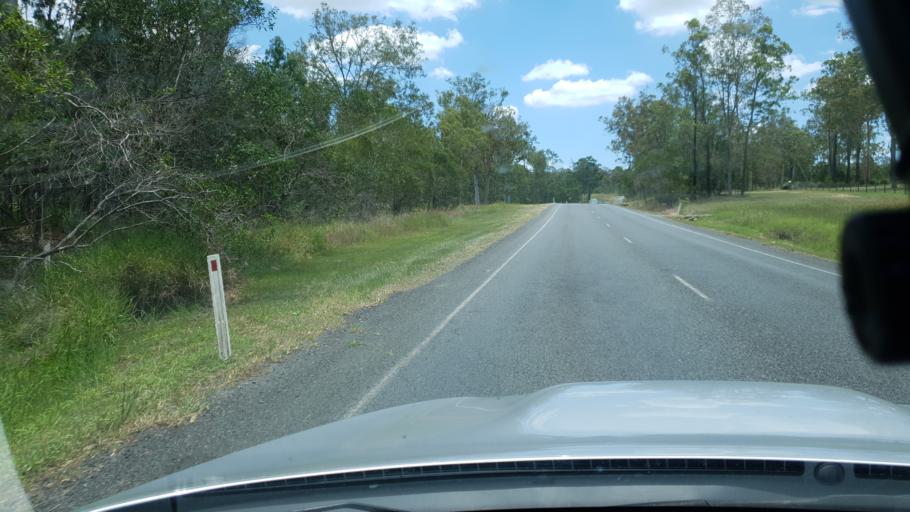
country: AU
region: Queensland
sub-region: Logan
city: North Maclean
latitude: -27.7514
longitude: 152.9866
